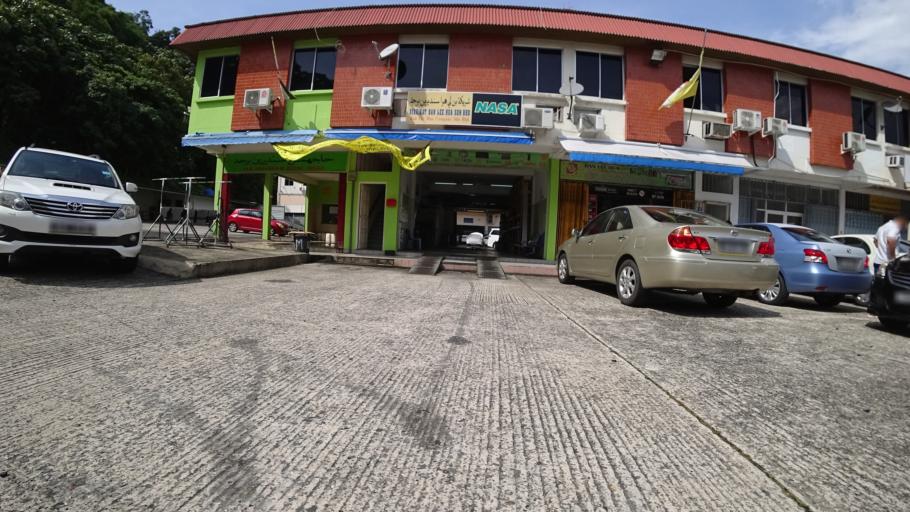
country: BN
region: Brunei and Muara
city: Bandar Seri Begawan
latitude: 4.8573
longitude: 114.8910
